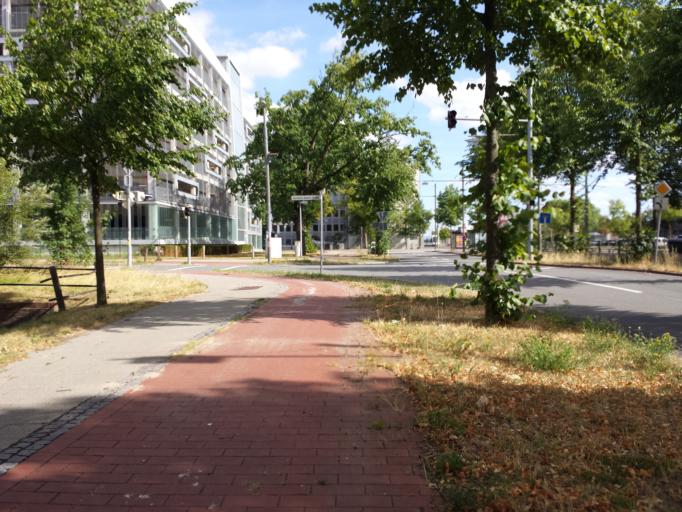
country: DE
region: Bremen
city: Bremen
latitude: 53.0511
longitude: 8.7893
